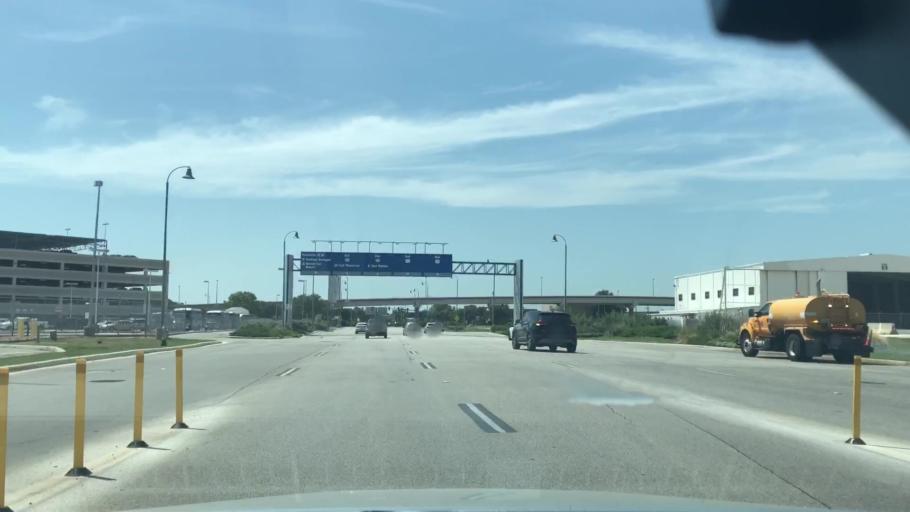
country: US
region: Texas
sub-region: Bexar County
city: Castle Hills
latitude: 29.5271
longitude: -98.4770
